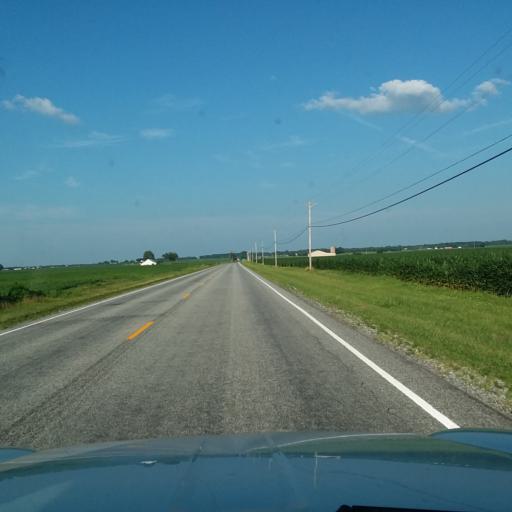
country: US
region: Indiana
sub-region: Johnson County
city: Franklin
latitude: 39.4111
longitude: -86.0524
